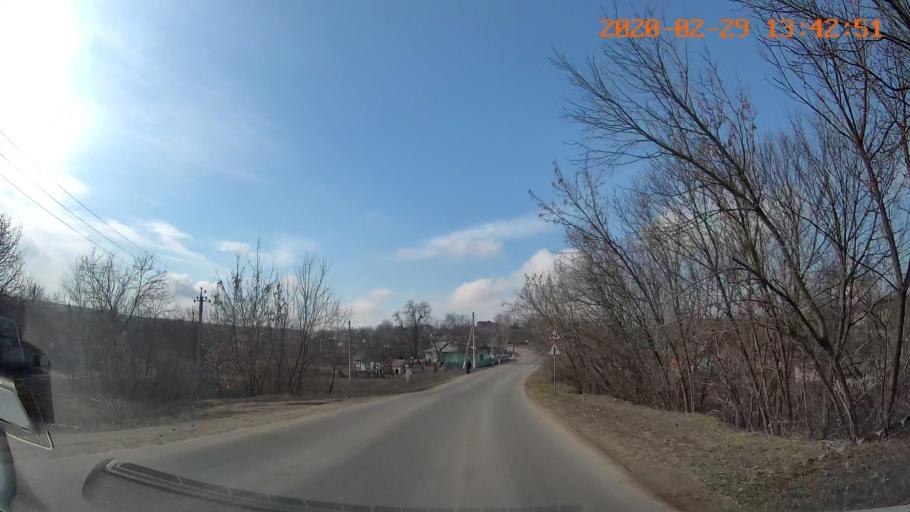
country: MD
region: Floresti
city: Leninskiy
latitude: 47.8408
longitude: 28.5414
